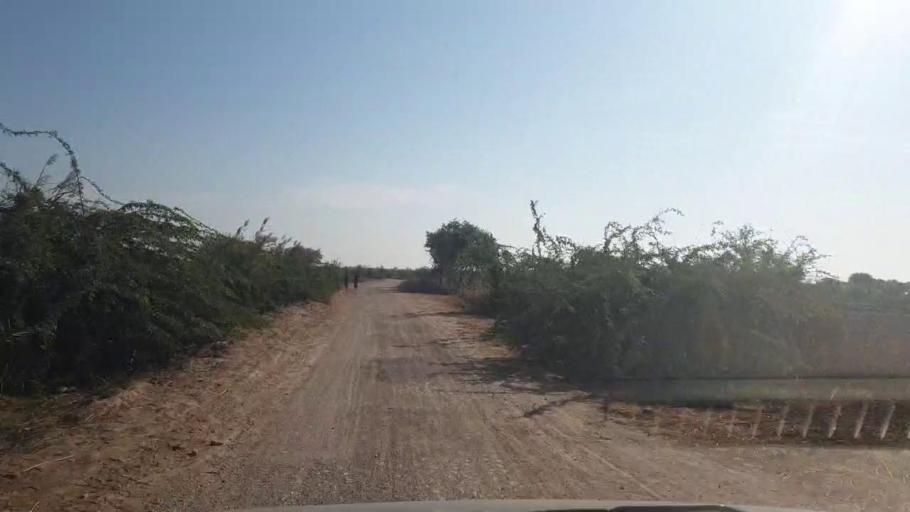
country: PK
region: Sindh
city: Rajo Khanani
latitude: 24.9716
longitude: 68.7732
